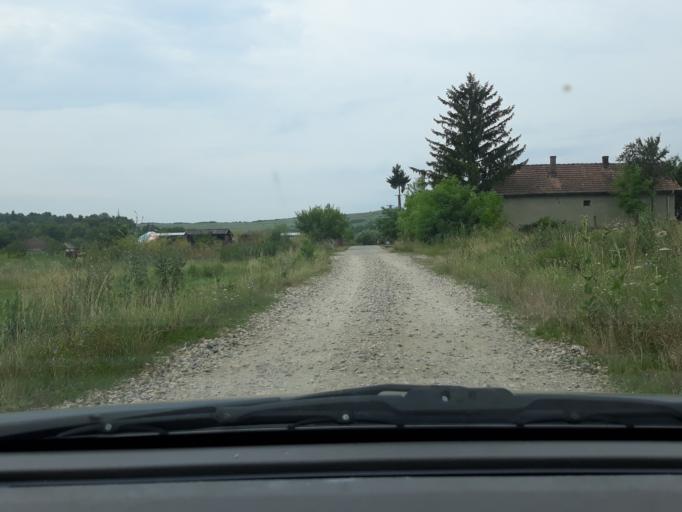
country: RO
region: Salaj
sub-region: Comuna Criseni
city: Criseni
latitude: 47.2638
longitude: 23.0664
